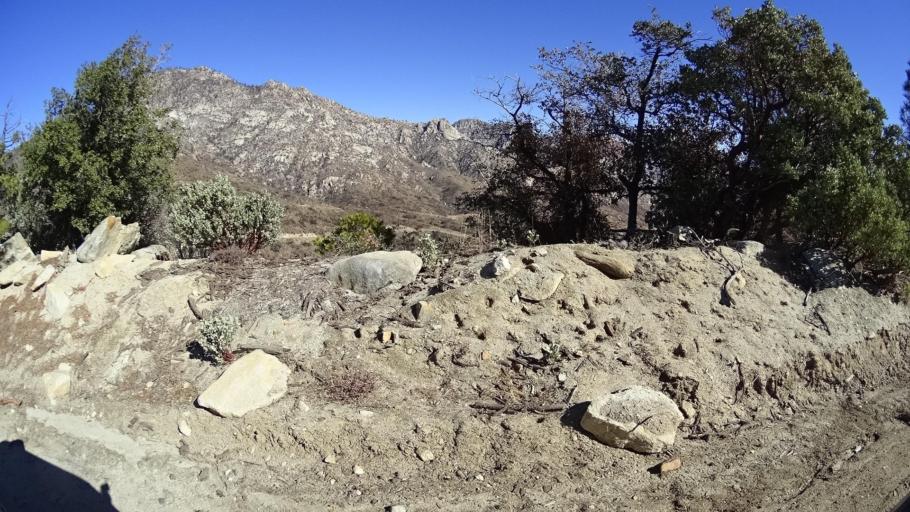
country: US
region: California
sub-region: Kern County
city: Alta Sierra
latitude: 35.7185
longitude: -118.5300
